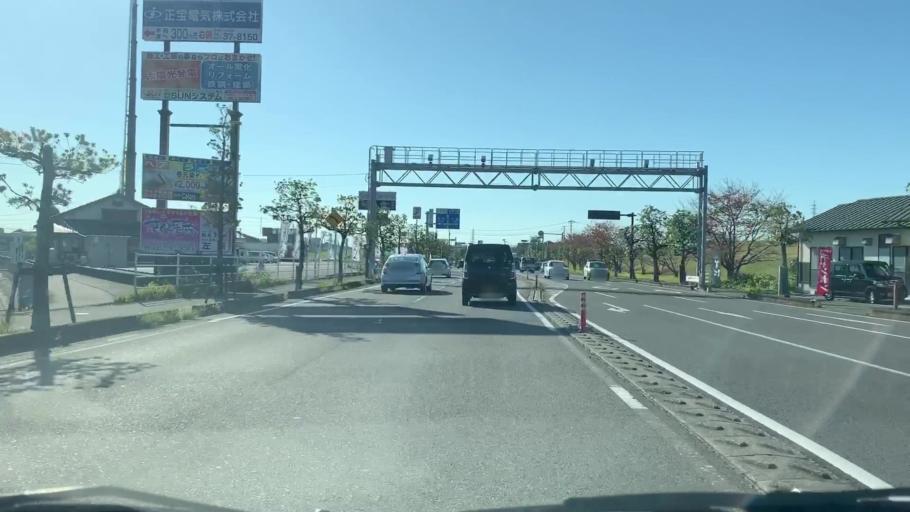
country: JP
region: Saga Prefecture
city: Saga-shi
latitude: 33.3120
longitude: 130.2760
